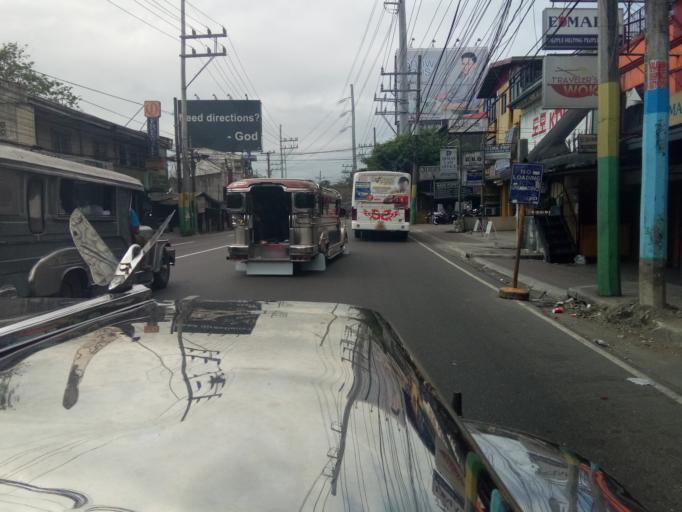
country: PH
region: Calabarzon
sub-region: Province of Cavite
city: Dasmarinas
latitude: 14.3030
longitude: 120.9541
